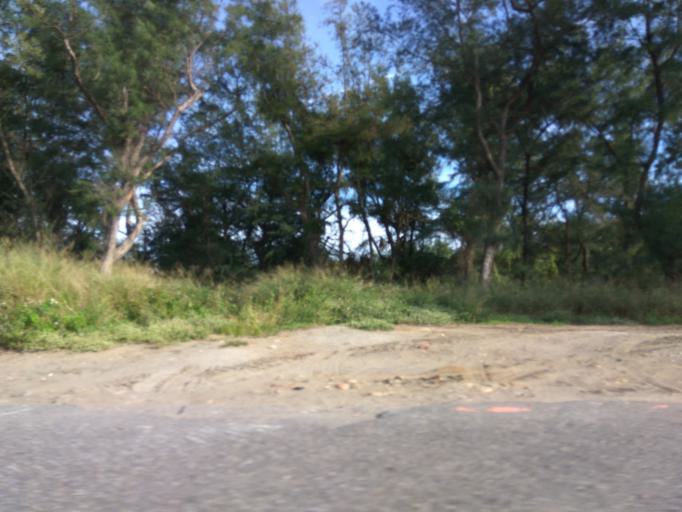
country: TW
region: Taiwan
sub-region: Hsinchu
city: Zhubei
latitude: 24.9732
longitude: 121.0143
